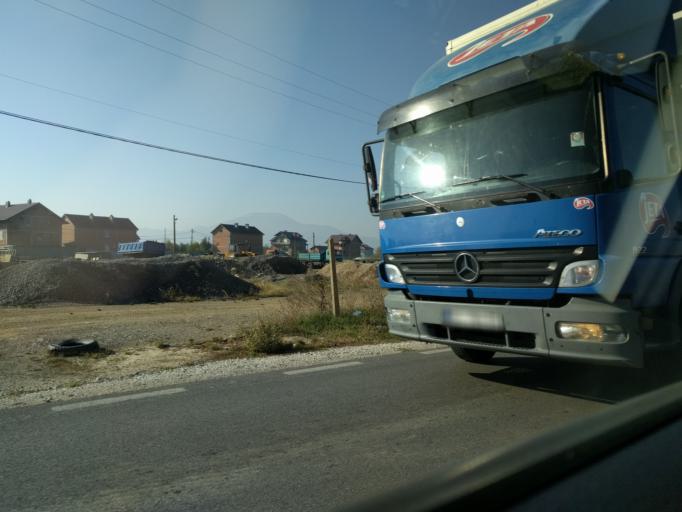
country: XK
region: Prizren
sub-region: Prizren
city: Prizren
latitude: 42.2489
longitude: 20.7337
